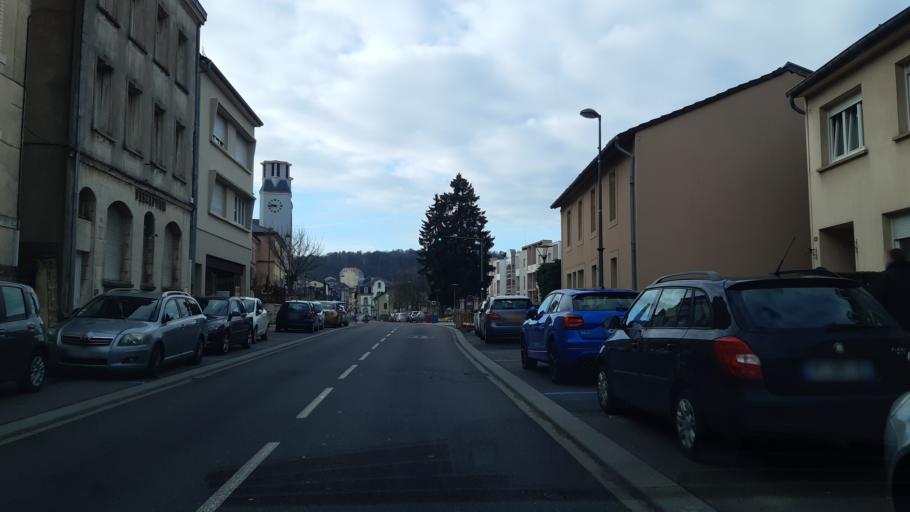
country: FR
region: Lorraine
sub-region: Departement de la Moselle
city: Audun-le-Tiche
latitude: 49.4736
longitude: 5.9572
